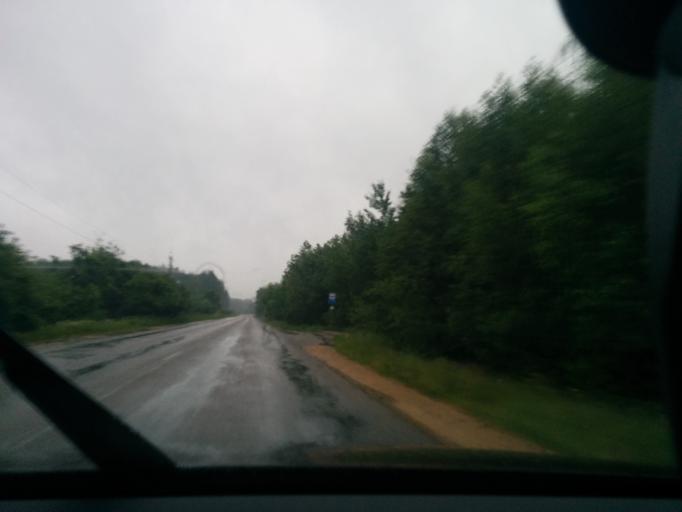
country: LV
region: Stopini
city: Ulbroka
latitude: 56.9149
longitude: 24.3356
